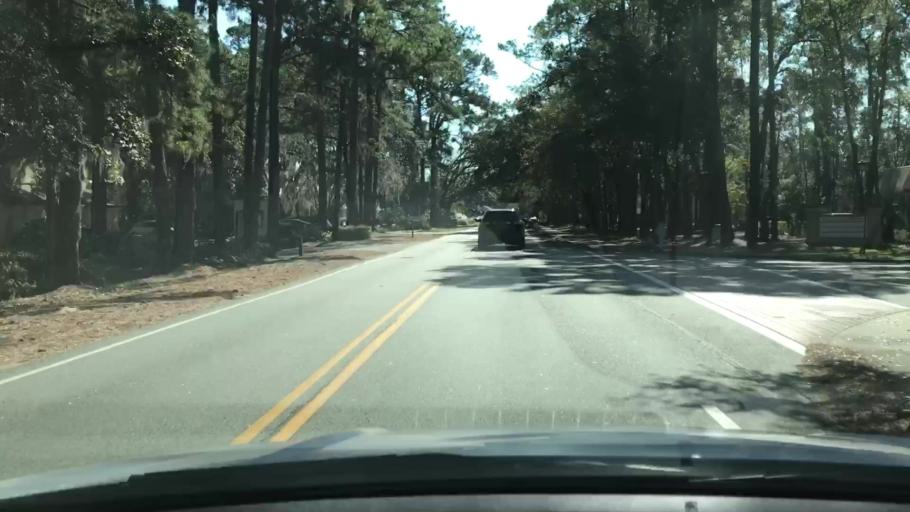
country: US
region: South Carolina
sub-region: Beaufort County
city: Hilton Head Island
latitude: 32.2203
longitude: -80.7045
